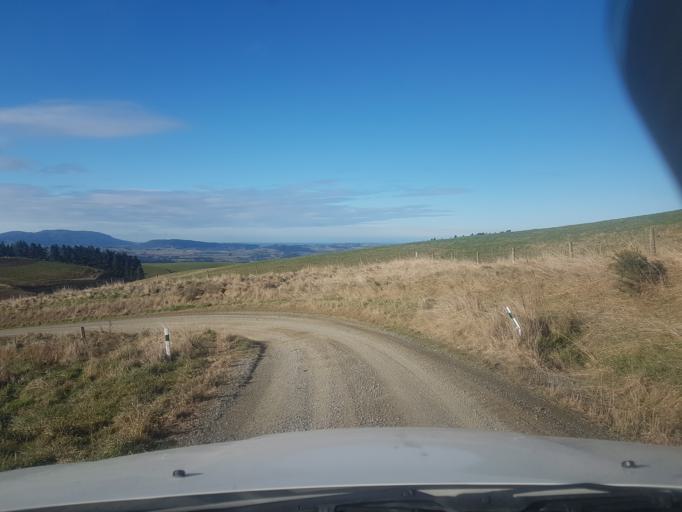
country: NZ
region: Canterbury
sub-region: Timaru District
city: Pleasant Point
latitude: -44.1674
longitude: 170.8917
